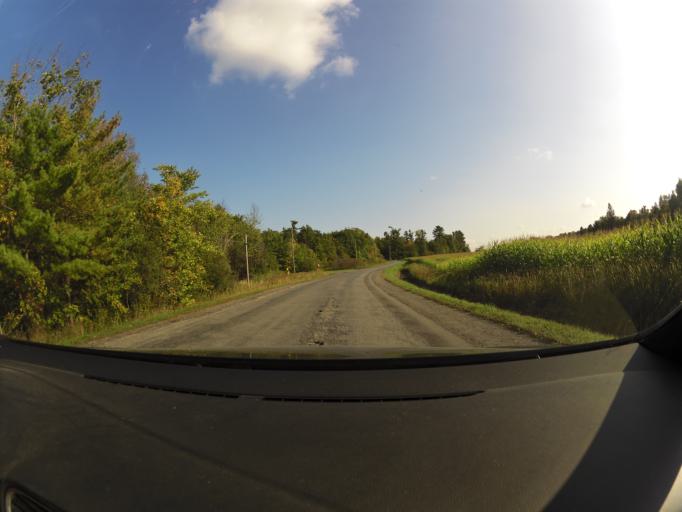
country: CA
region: Ontario
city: Arnprior
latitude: 45.4066
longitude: -76.2083
